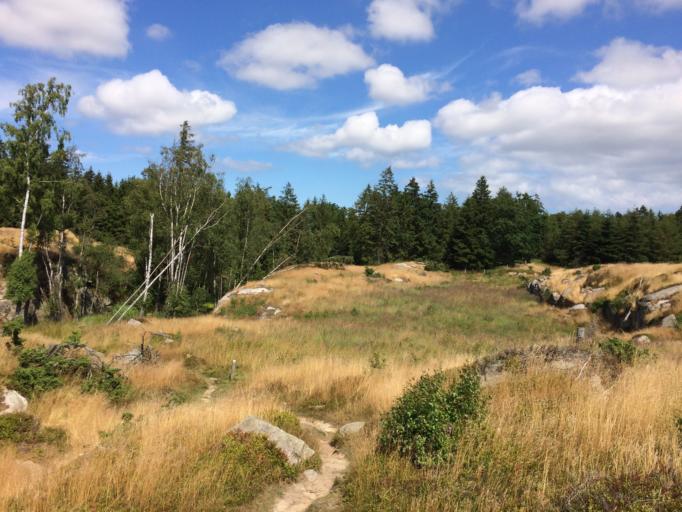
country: DK
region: Capital Region
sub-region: Bornholm Kommune
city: Nexo
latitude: 55.0970
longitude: 15.0884
